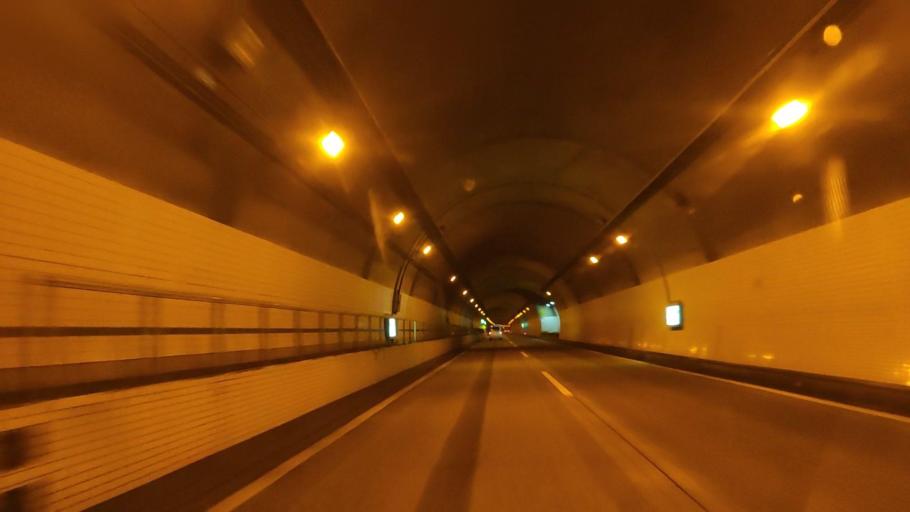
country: JP
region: Niigata
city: Joetsu
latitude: 37.1338
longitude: 138.0597
